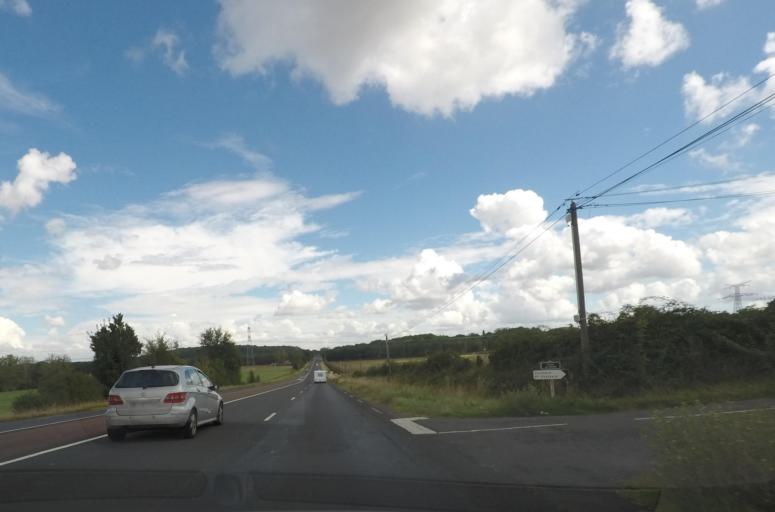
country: FR
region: Pays de la Loire
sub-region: Departement de la Sarthe
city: Cerans-Foulletourte
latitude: 47.8355
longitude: 0.0823
